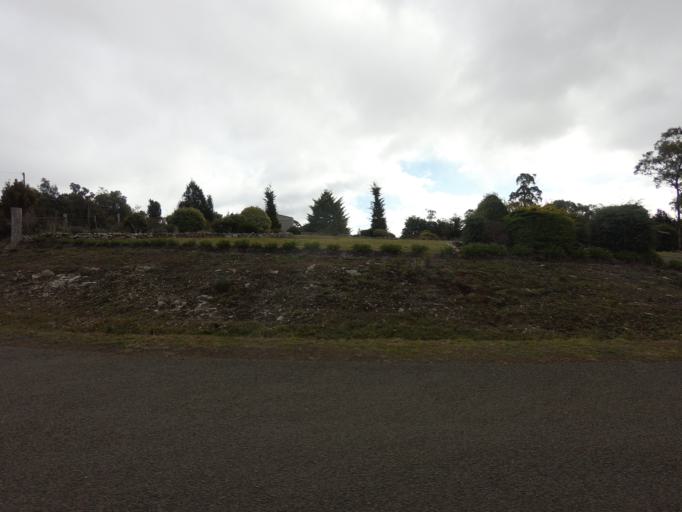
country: AU
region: Tasmania
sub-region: Sorell
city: Sorell
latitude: -42.5348
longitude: 147.9123
